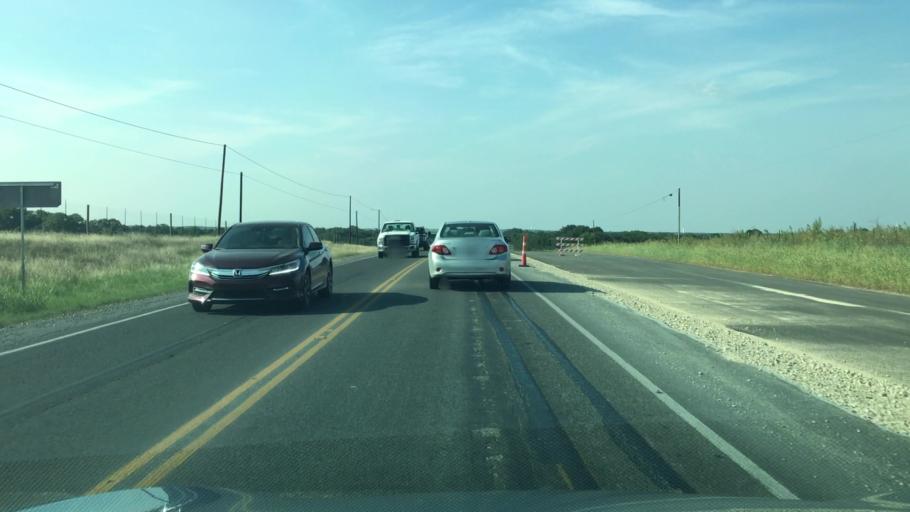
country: US
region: Texas
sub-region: Hays County
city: Buda
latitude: 30.0512
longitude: -97.8746
